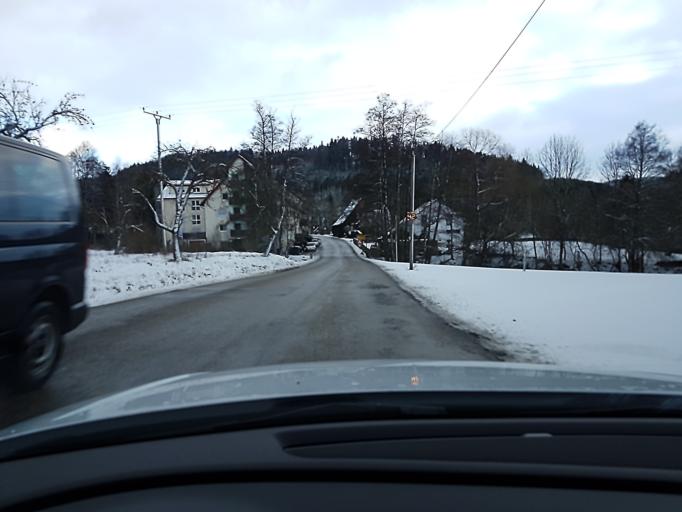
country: DE
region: Baden-Wuerttemberg
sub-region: Regierungsbezirk Stuttgart
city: Kaisersbach
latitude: 48.9602
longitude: 9.6590
